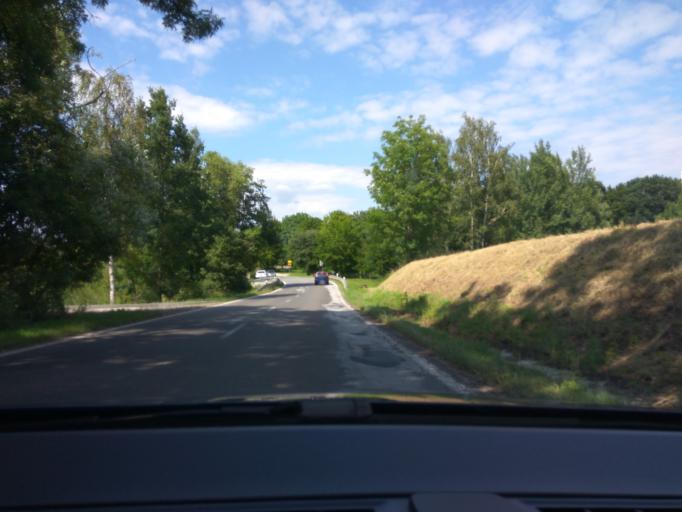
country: CZ
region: Jihocesky
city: Milevsko
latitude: 49.4427
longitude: 14.3596
